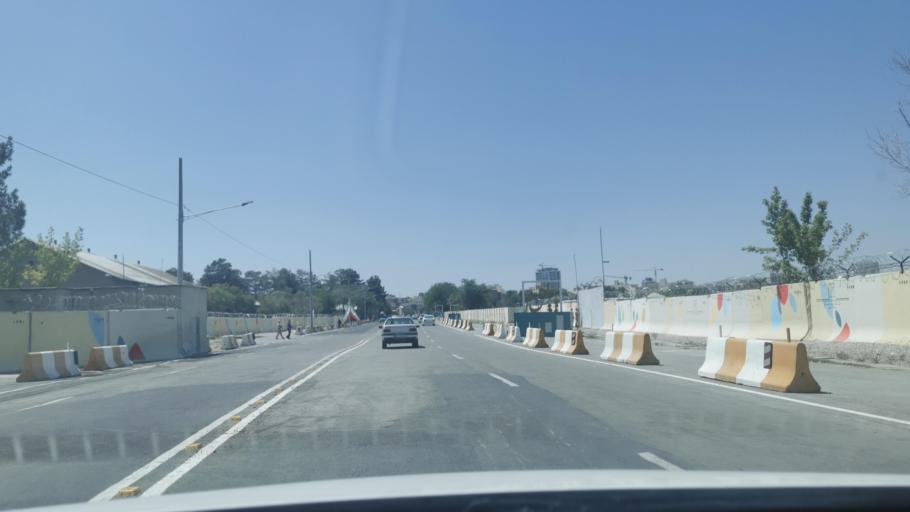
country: IR
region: Razavi Khorasan
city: Mashhad
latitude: 36.2739
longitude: 59.5821
